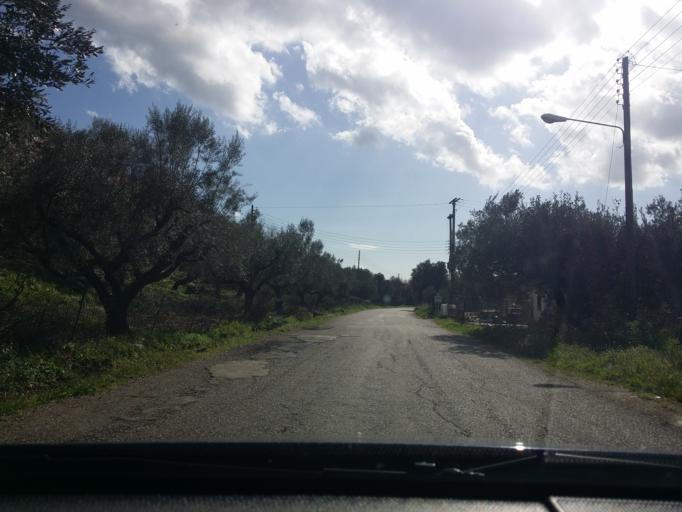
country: GR
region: West Greece
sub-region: Nomos Aitolias kai Akarnanias
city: Astakos
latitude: 38.5886
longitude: 21.0896
